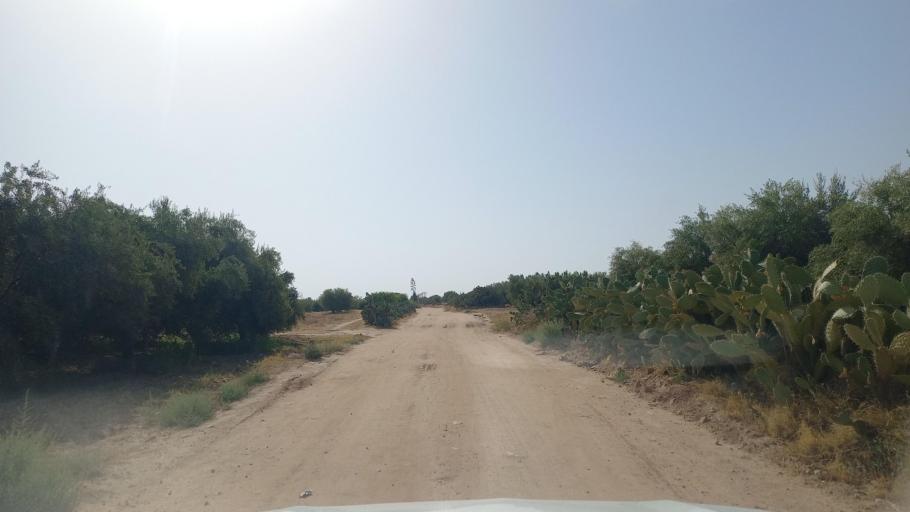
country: TN
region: Al Qasrayn
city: Kasserine
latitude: 35.2503
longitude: 9.0313
